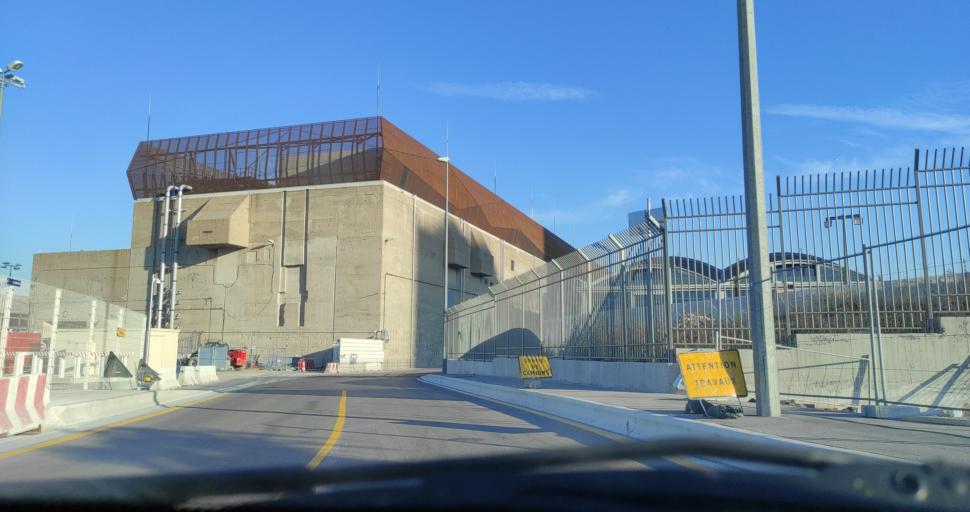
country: FR
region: Provence-Alpes-Cote d'Azur
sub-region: Departement des Bouches-du-Rhone
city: Marseille 16
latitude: 43.3375
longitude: 5.3482
